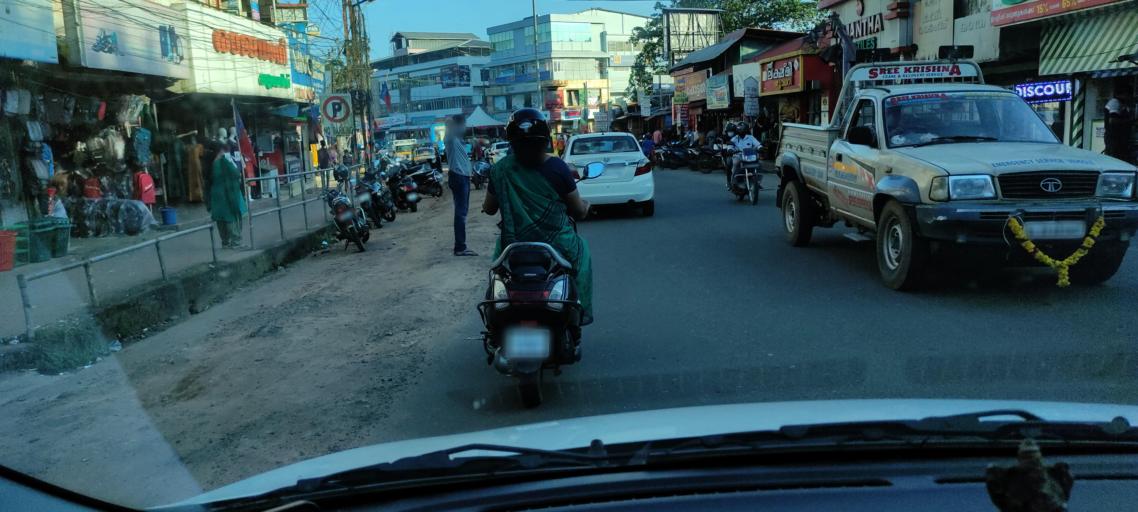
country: IN
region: Kerala
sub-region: Pattanamtitta
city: Adur
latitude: 9.1539
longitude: 76.7330
